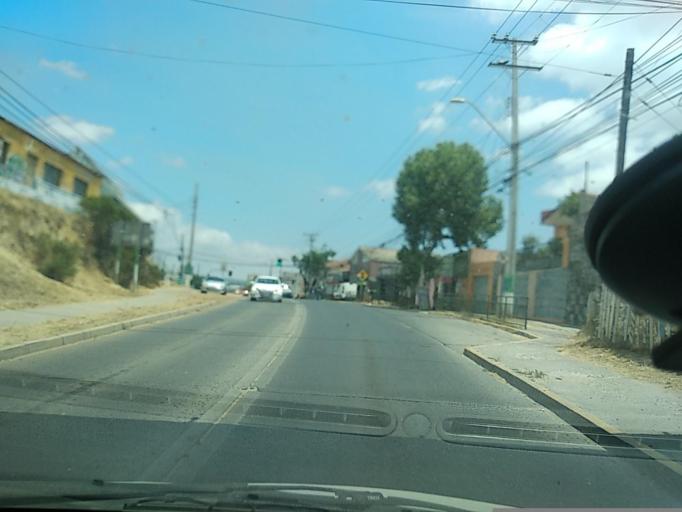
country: CL
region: Valparaiso
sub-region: Provincia de Marga Marga
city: Quilpue
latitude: -33.0423
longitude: -71.4298
